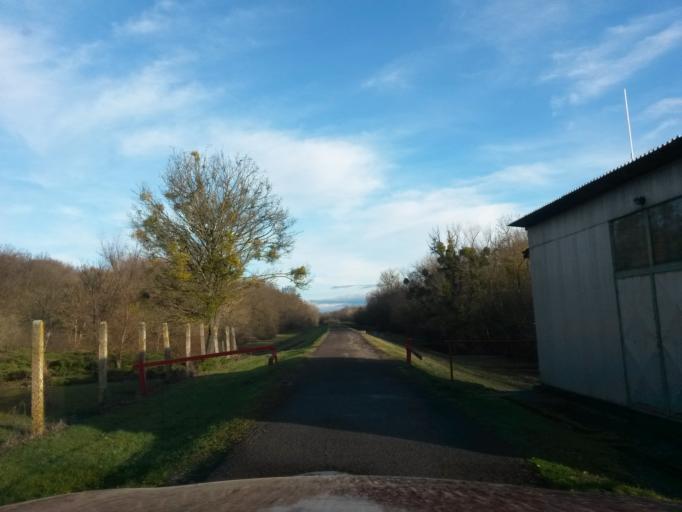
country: SK
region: Kosicky
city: Cierna nad Tisou
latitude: 48.5185
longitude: 22.0286
